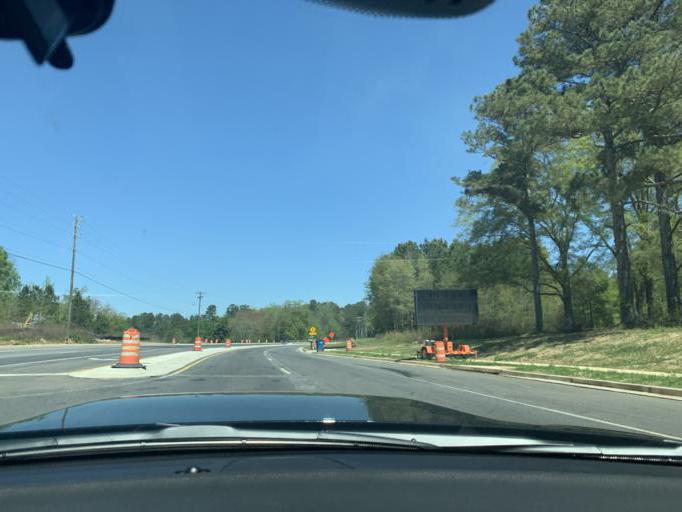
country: US
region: Georgia
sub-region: Forsyth County
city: Cumming
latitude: 34.2137
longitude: -84.1986
